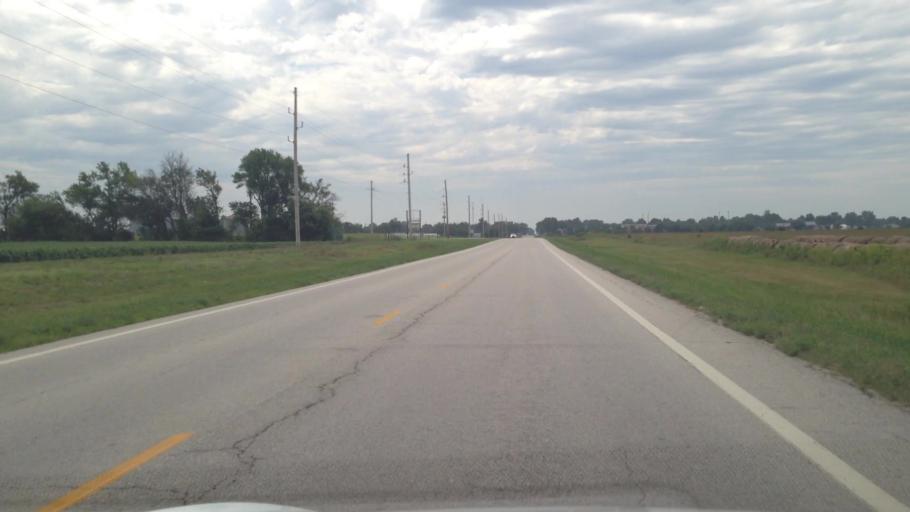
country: US
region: Kansas
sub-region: Allen County
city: Iola
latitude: 37.9302
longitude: -95.1701
